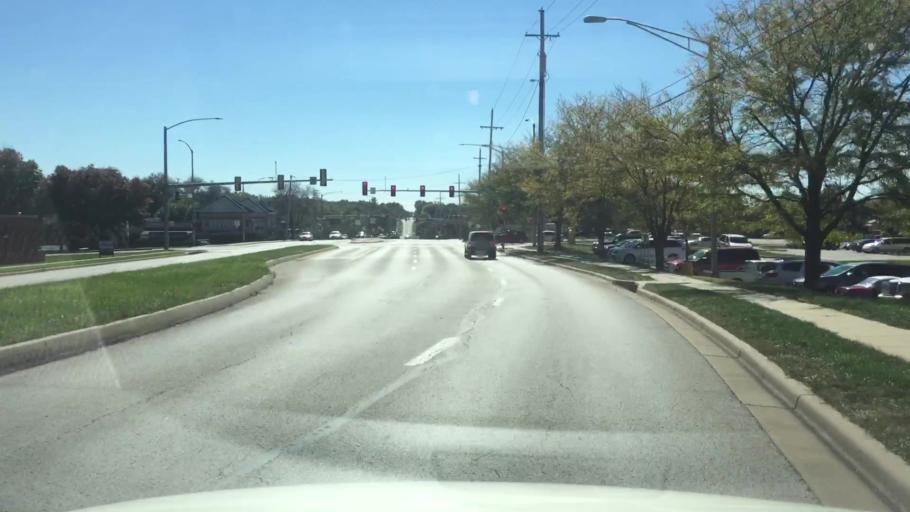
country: US
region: Kansas
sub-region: Johnson County
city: Shawnee
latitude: 39.0162
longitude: -94.7426
